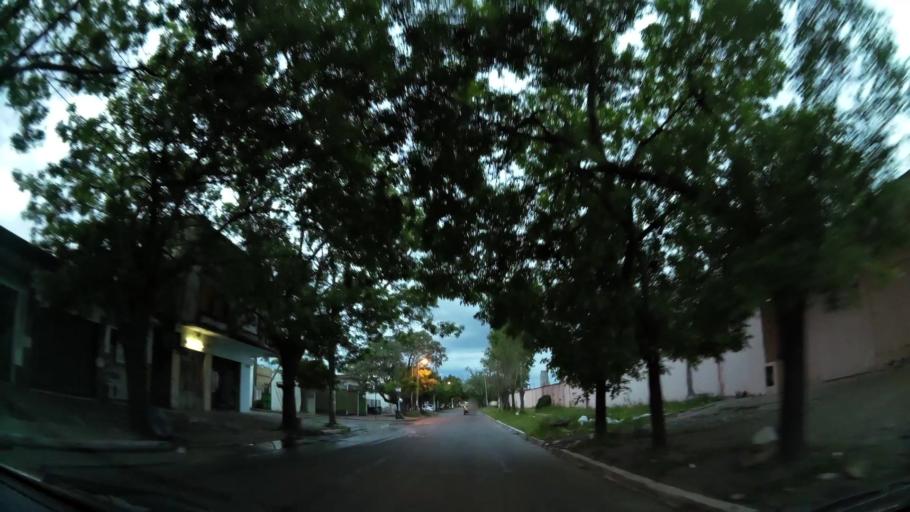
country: AR
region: Buenos Aires
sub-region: Partido de Quilmes
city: Quilmes
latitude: -34.7430
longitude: -58.2275
